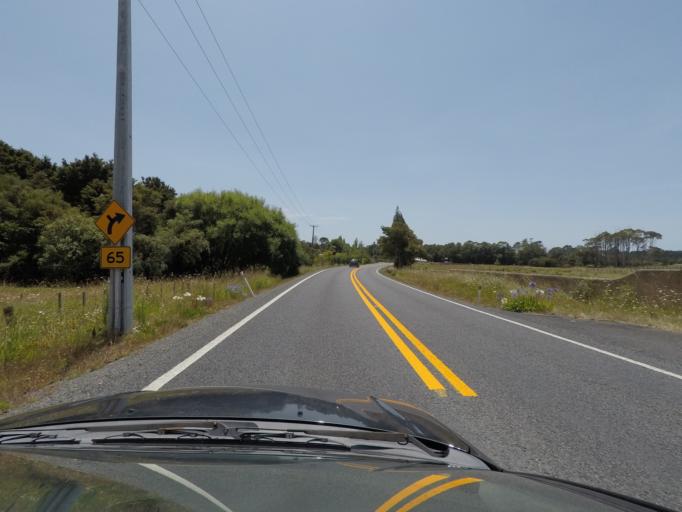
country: NZ
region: Auckland
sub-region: Auckland
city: Warkworth
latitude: -36.3707
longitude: 174.6814
